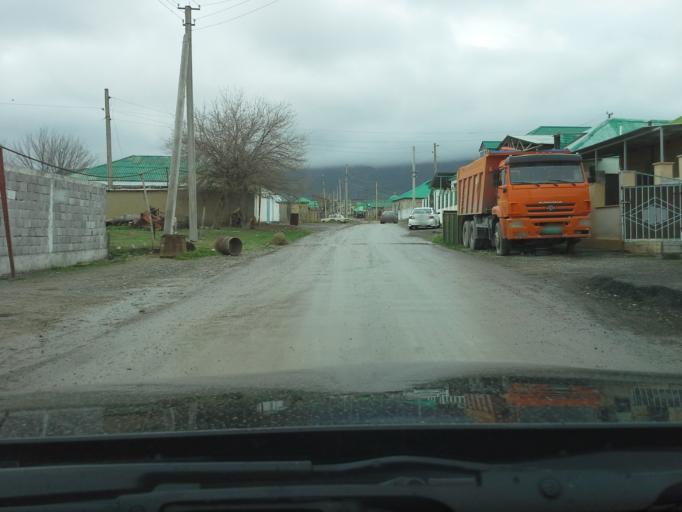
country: TM
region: Ahal
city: Abadan
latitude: 37.9687
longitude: 58.2103
